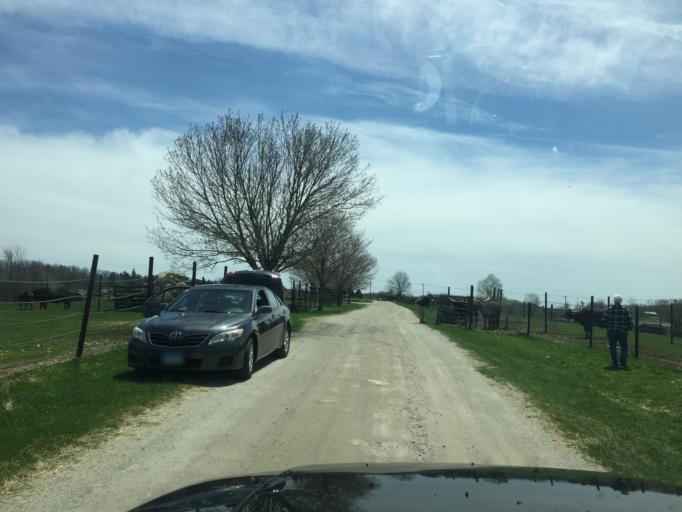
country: US
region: Connecticut
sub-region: Litchfield County
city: West Torrington
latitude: 41.8338
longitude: -73.1951
